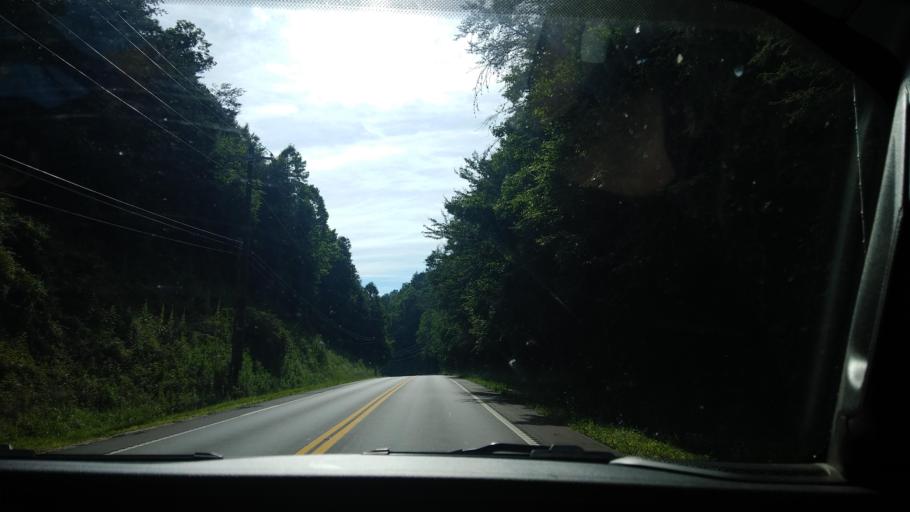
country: US
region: Tennessee
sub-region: Sevier County
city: Gatlinburg
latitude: 35.7513
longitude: -83.3906
